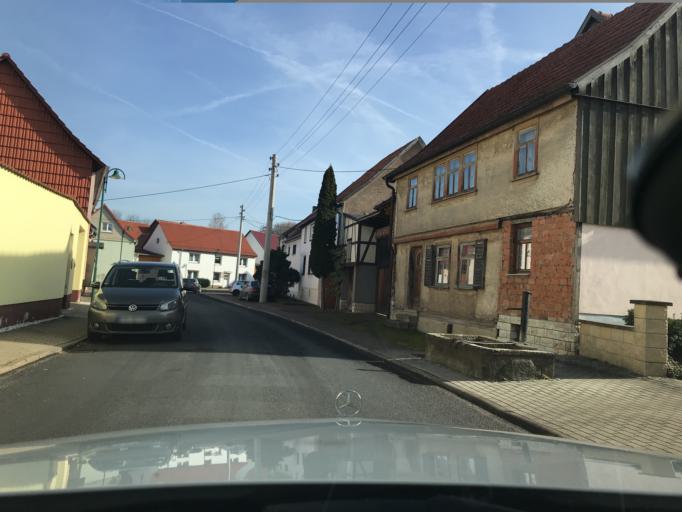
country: DE
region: Thuringia
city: Ernstroda
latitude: 50.9008
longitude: 10.6315
